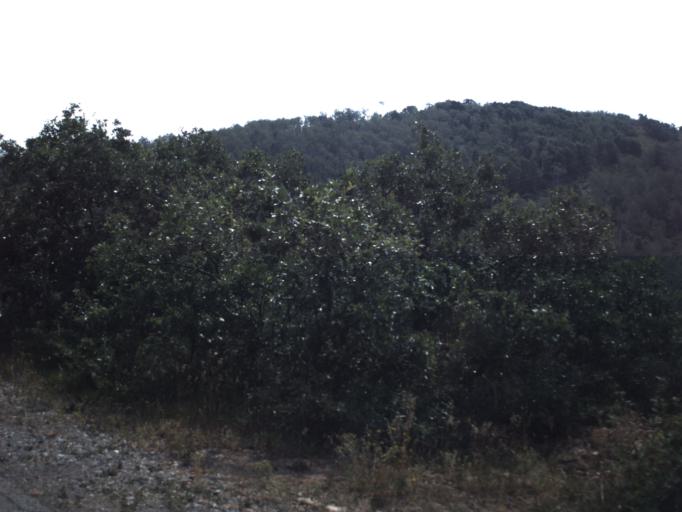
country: US
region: Utah
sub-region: Summit County
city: Summit Park
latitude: 40.8278
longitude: -111.6561
